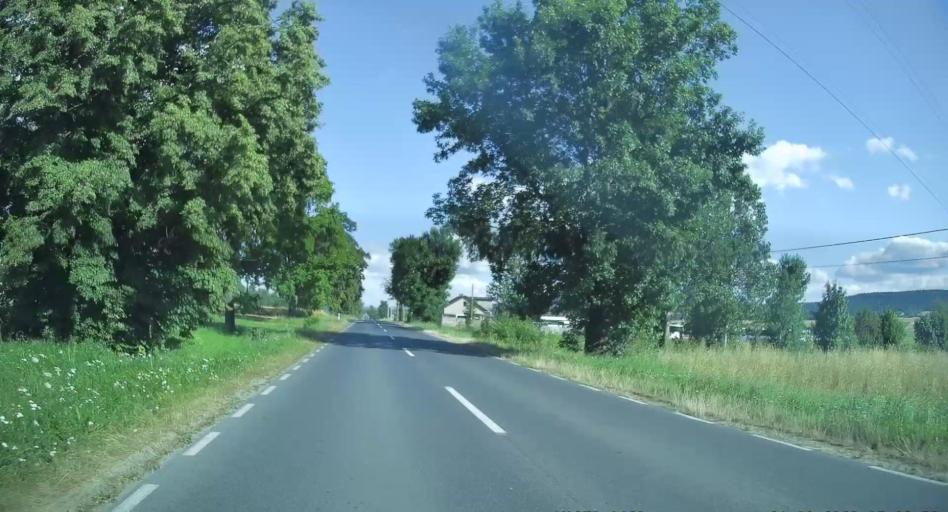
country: PL
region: Swietokrzyskie
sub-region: Powiat kielecki
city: Bodzentyn
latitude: 50.9570
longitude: 20.9127
